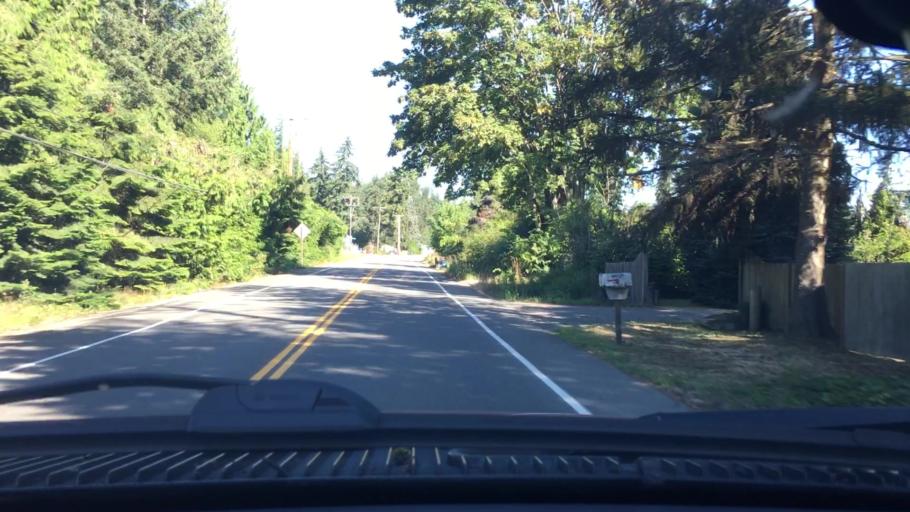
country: US
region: Washington
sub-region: King County
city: Covington
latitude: 47.3442
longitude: -122.1352
